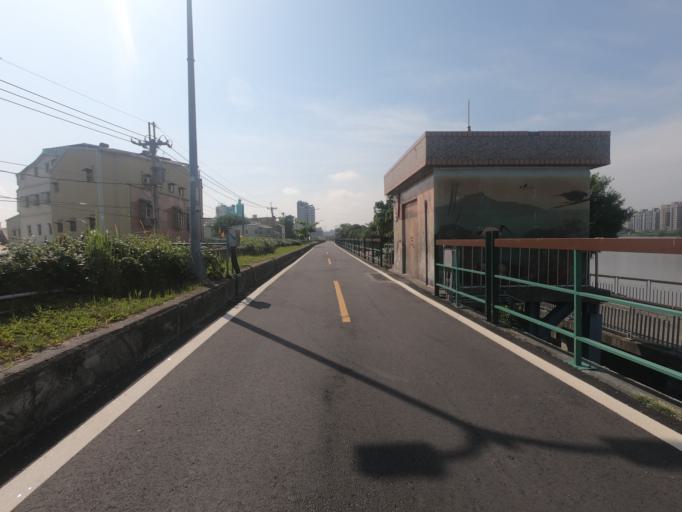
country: TW
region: Taipei
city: Taipei
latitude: 25.0955
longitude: 121.4944
